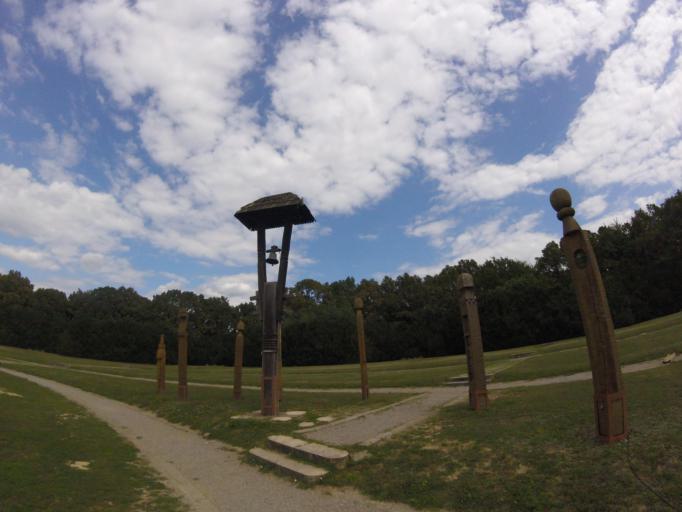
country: HU
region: Baranya
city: Mohacs
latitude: 45.9413
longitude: 18.6472
